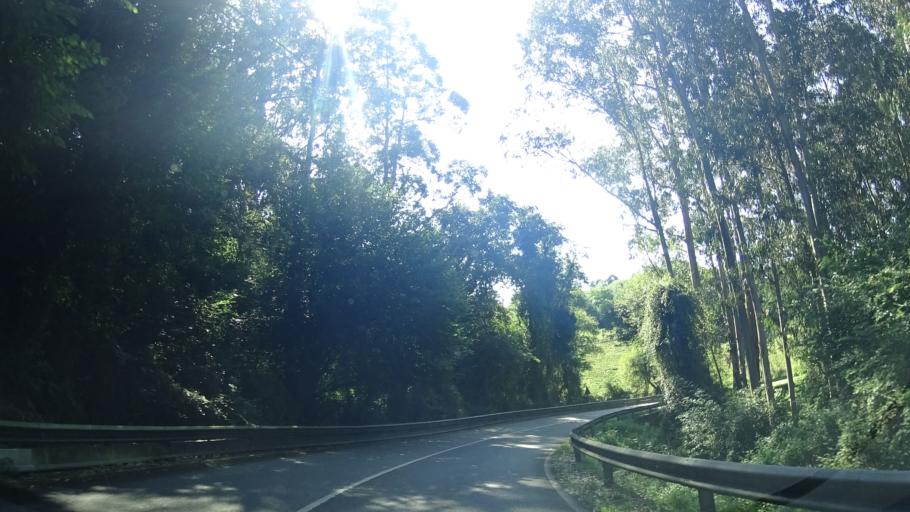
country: ES
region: Asturias
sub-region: Province of Asturias
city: Ribadesella
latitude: 43.4633
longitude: -5.0909
